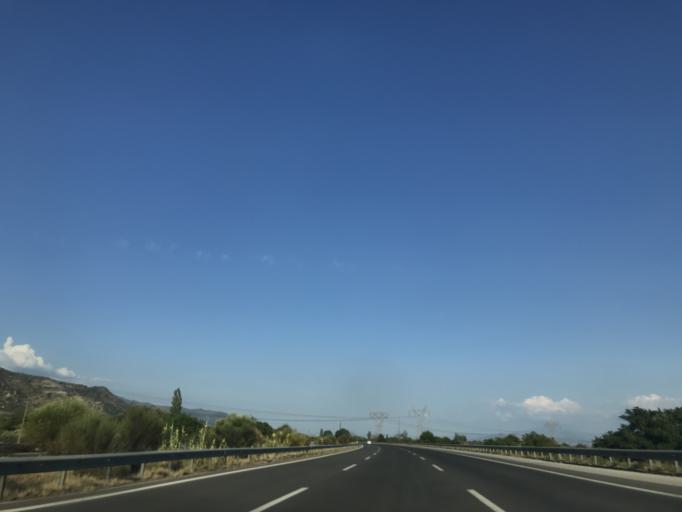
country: TR
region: Aydin
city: Incirliova
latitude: 37.8688
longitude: 27.7179
